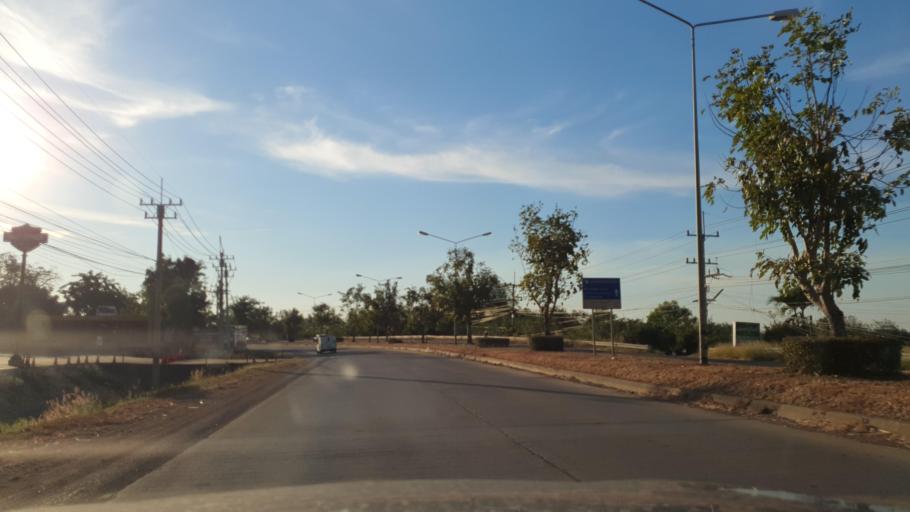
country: TH
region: Khon Kaen
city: Khon Kaen
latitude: 16.4374
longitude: 102.9009
